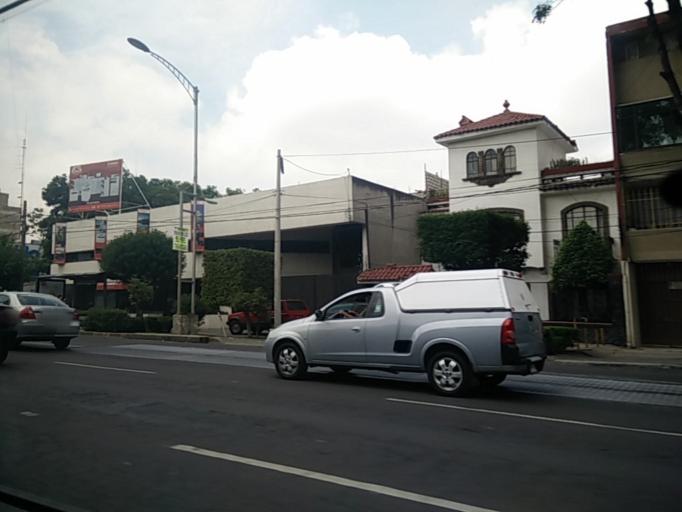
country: MX
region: Mexico City
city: Colonia del Valle
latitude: 19.3881
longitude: -99.1568
